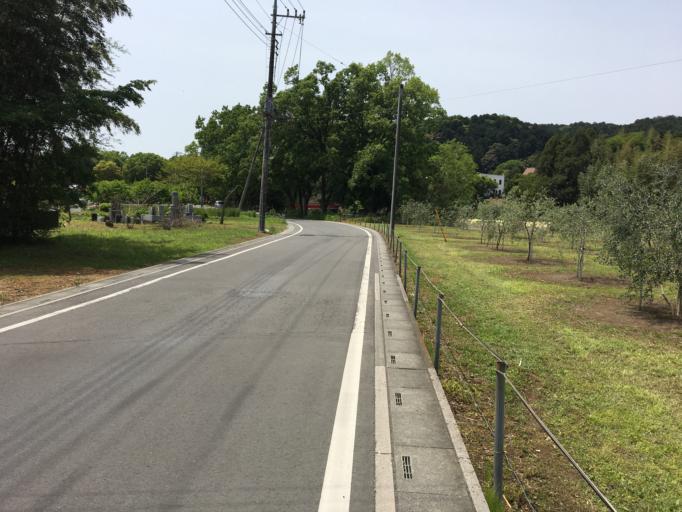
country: JP
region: Saitama
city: Morohongo
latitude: 35.8978
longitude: 139.3271
